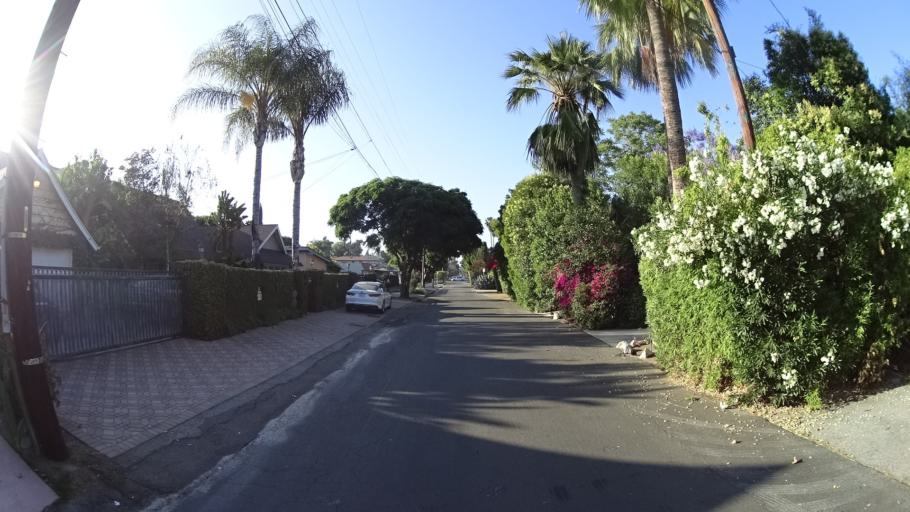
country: US
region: California
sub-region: Los Angeles County
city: Van Nuys
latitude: 34.1709
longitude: -118.4422
